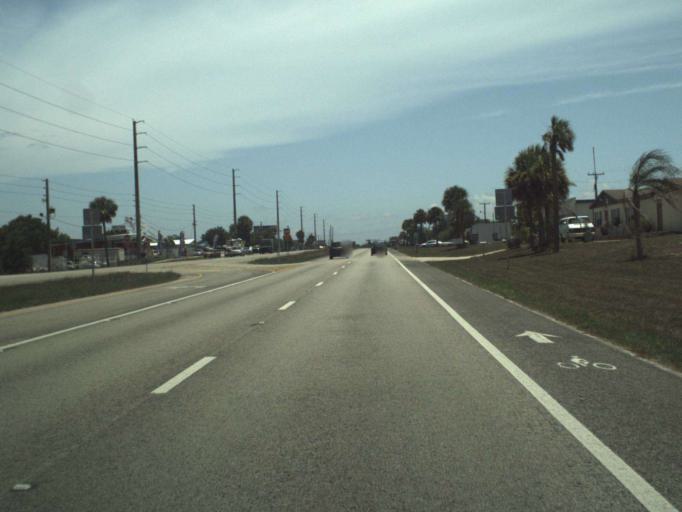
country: US
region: Florida
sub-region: Saint Lucie County
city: Fort Pierce North
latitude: 27.4893
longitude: -80.3426
